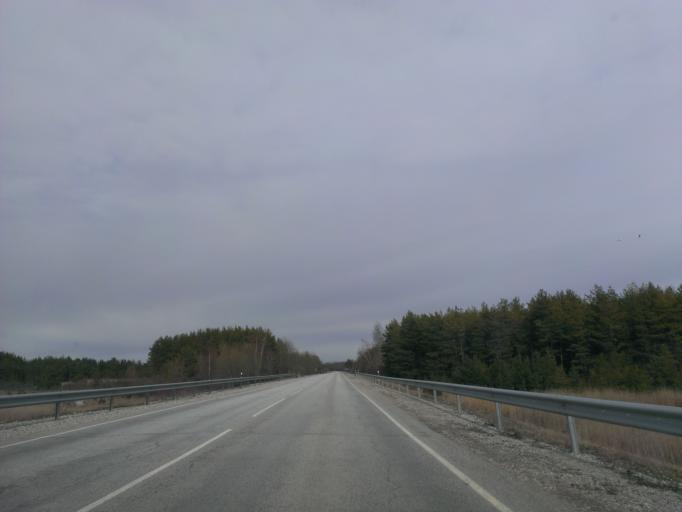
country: EE
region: Laeaene
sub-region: Lihula vald
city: Lihula
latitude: 58.5917
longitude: 23.5400
